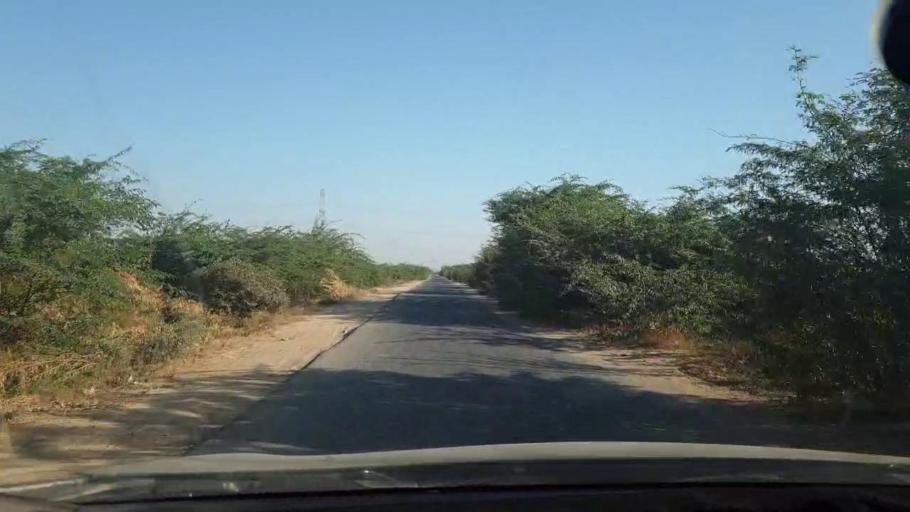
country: PK
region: Sindh
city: Malir Cantonment
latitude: 25.1578
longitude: 67.1929
